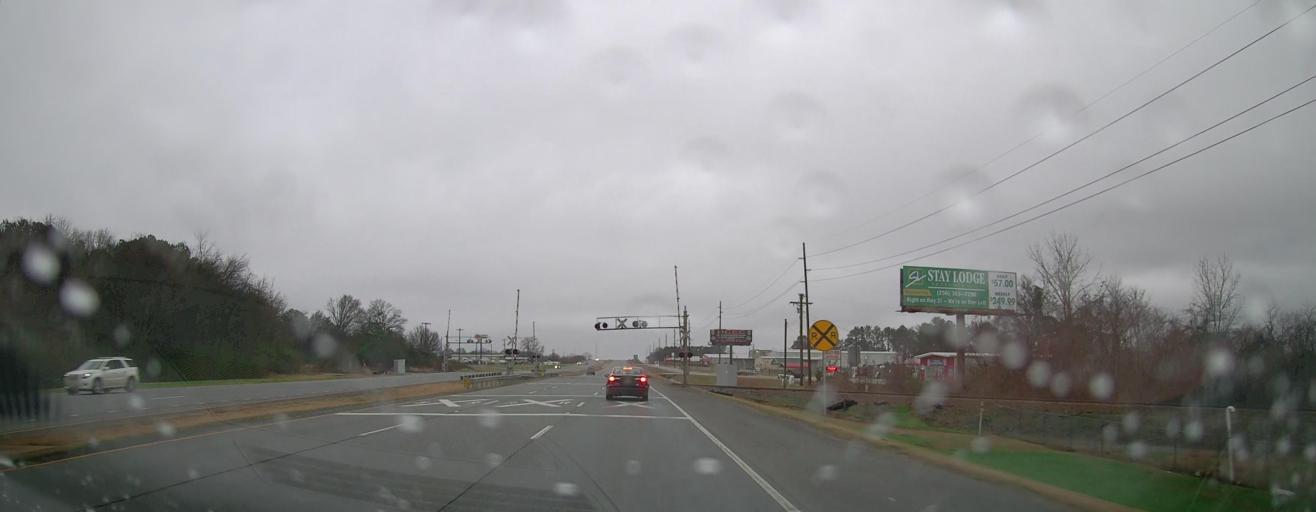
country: US
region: Alabama
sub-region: Morgan County
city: Decatur
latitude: 34.6165
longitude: -87.0311
